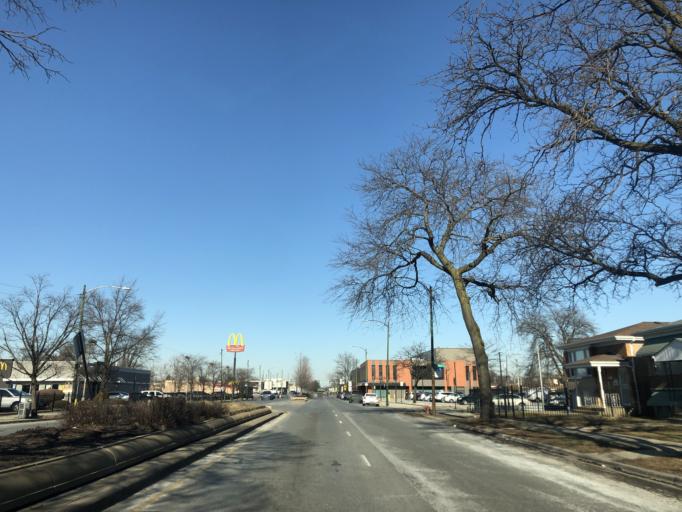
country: US
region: Illinois
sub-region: Cook County
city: Evergreen Park
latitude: 41.7190
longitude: -87.6430
